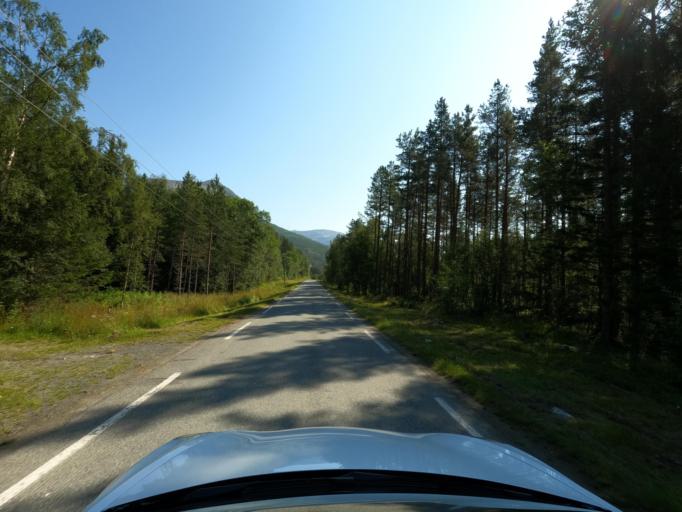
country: NO
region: Nordland
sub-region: Narvik
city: Narvik
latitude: 68.1982
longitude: 17.5504
